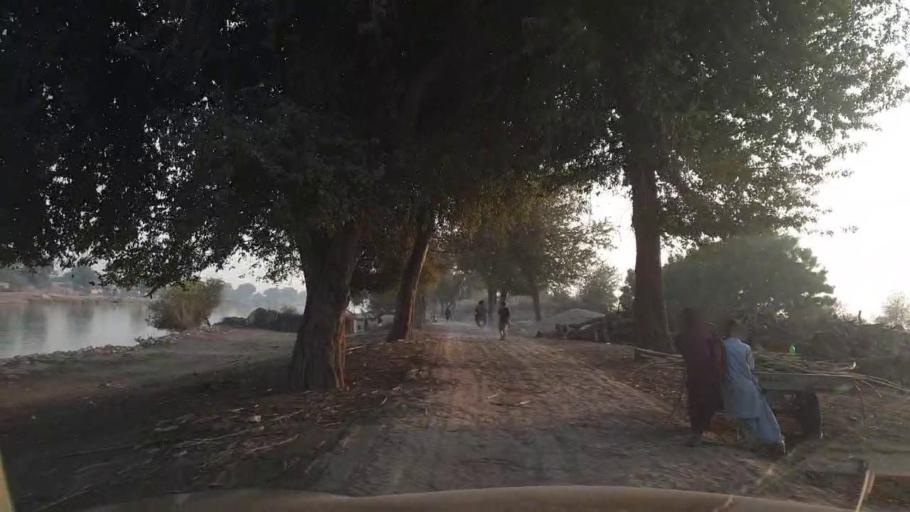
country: PK
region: Sindh
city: Ubauro
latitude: 28.3141
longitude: 69.7898
